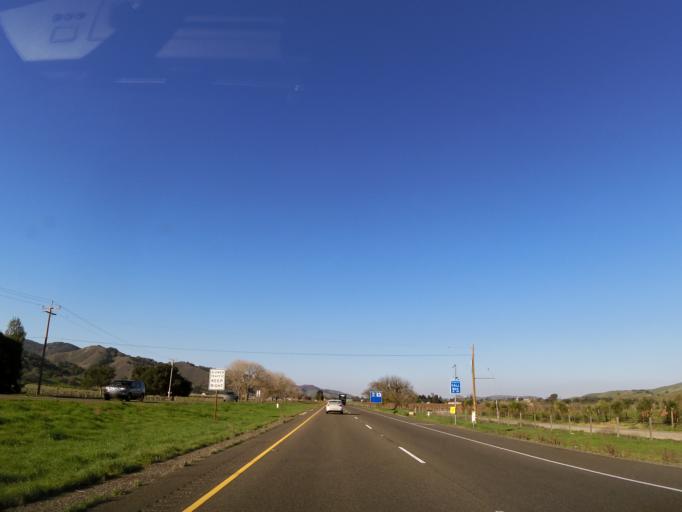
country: US
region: California
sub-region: Santa Barbara County
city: Los Alamos
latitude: 34.7368
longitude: -120.2562
